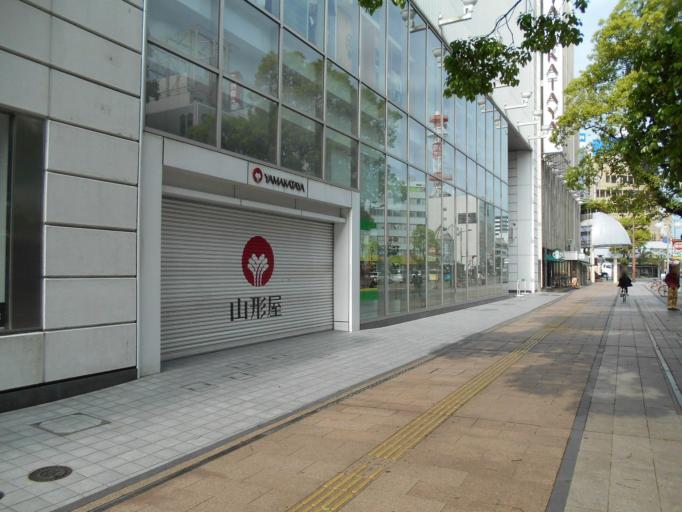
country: JP
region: Miyazaki
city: Miyazaki-shi
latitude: 31.9161
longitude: 131.4232
